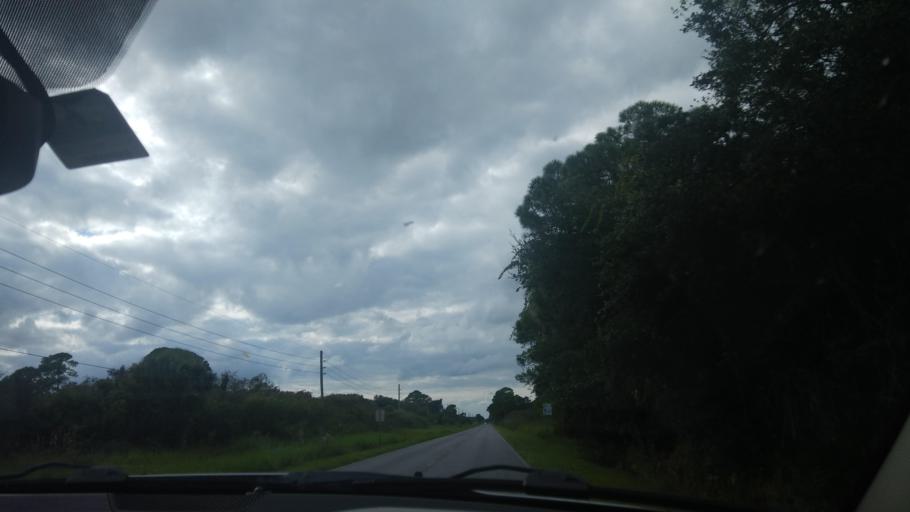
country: US
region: Florida
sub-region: Saint Lucie County
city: Lakewood Park
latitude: 27.5208
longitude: -80.3649
